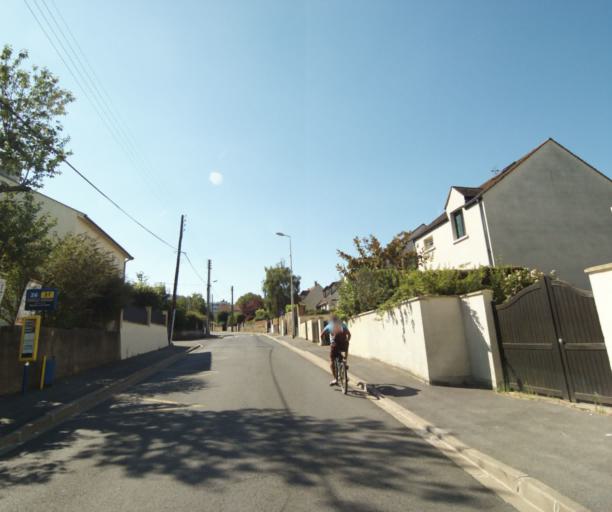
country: FR
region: Ile-de-France
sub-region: Departement de Seine-et-Marne
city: Gouvernes
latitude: 48.8712
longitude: 2.7003
